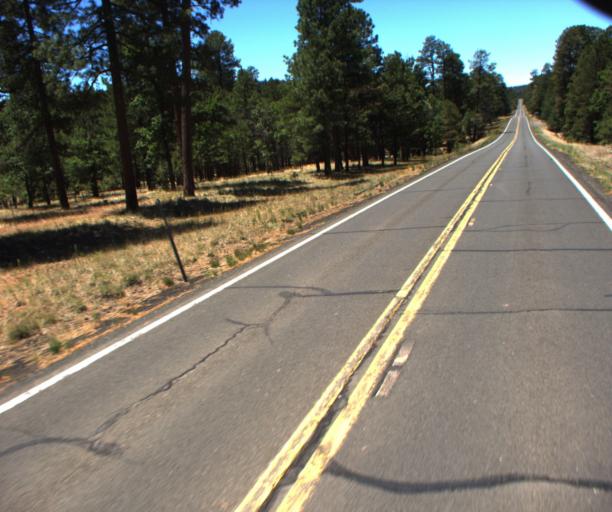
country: US
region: Arizona
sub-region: Gila County
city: Pine
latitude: 34.6077
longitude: -111.1950
